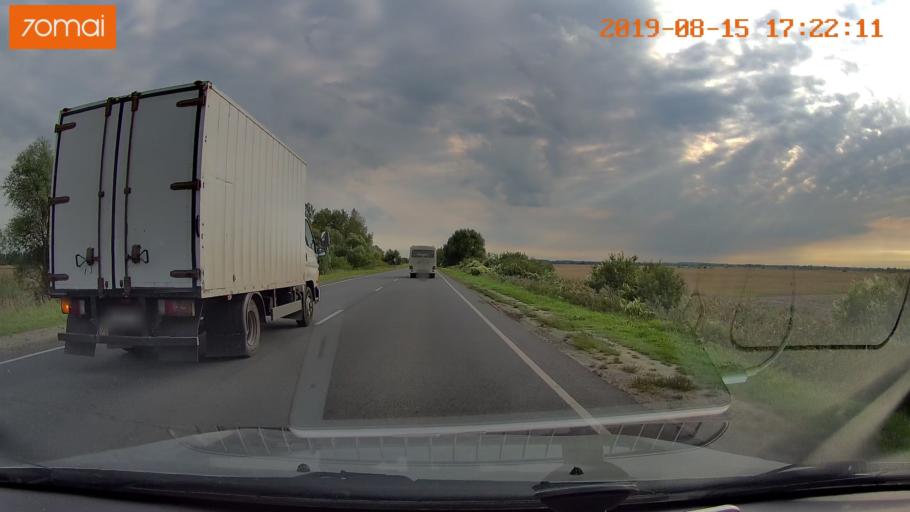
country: RU
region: Moskovskaya
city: Ashitkovo
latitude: 55.4167
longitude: 38.5643
